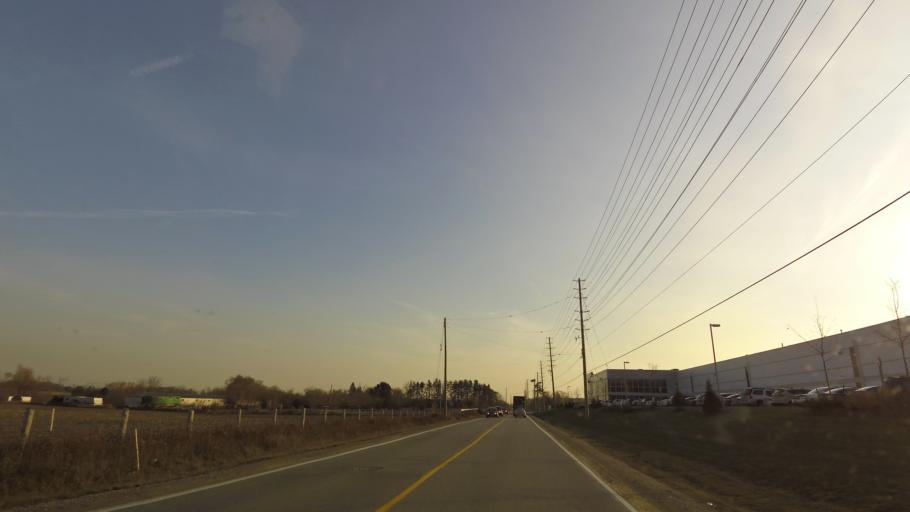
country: CA
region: Ontario
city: Vaughan
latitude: 43.8001
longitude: -79.6542
